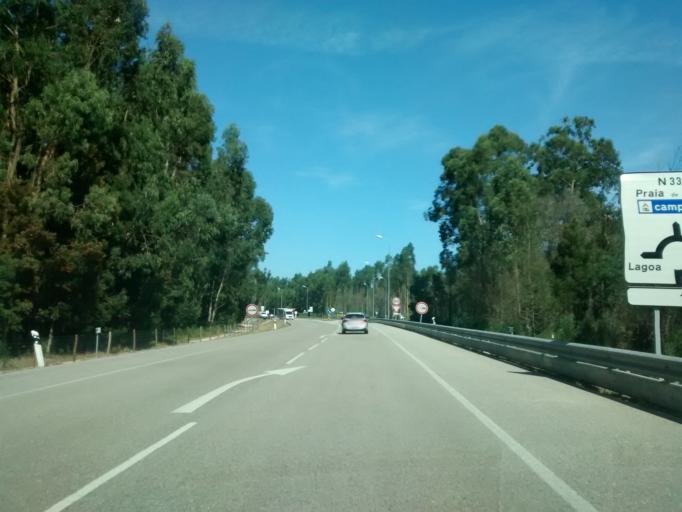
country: PT
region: Coimbra
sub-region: Mira
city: Mira
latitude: 40.4463
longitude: -8.7416
